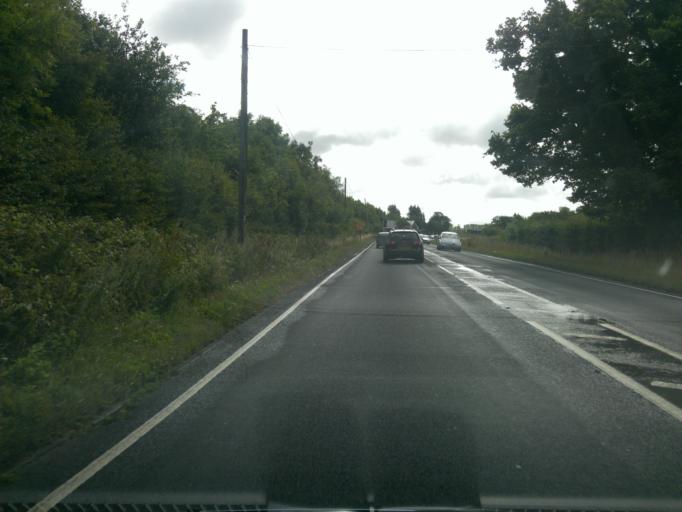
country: GB
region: England
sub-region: Essex
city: Great Bentley
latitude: 51.8637
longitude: 1.0874
